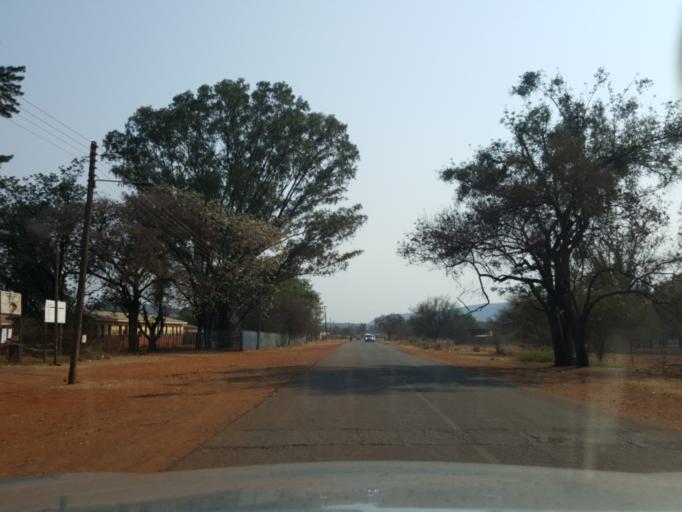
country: BW
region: South East
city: Lobatse
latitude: -25.3186
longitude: 25.7956
